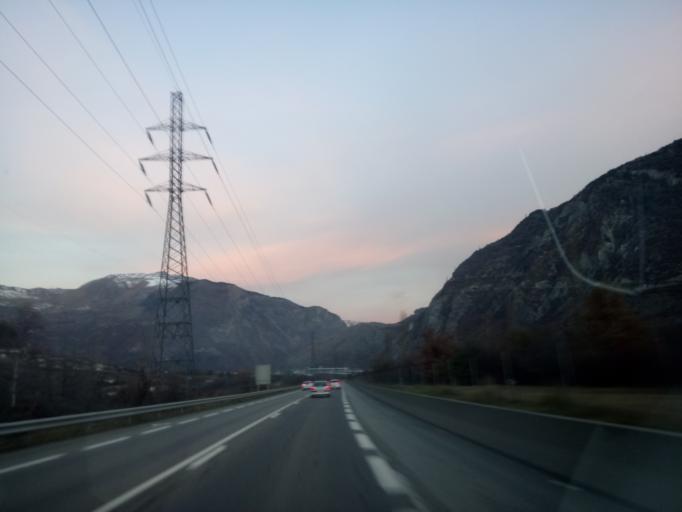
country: FR
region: Rhone-Alpes
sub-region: Departement de la Savoie
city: Villargondran
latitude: 45.2556
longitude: 6.3905
